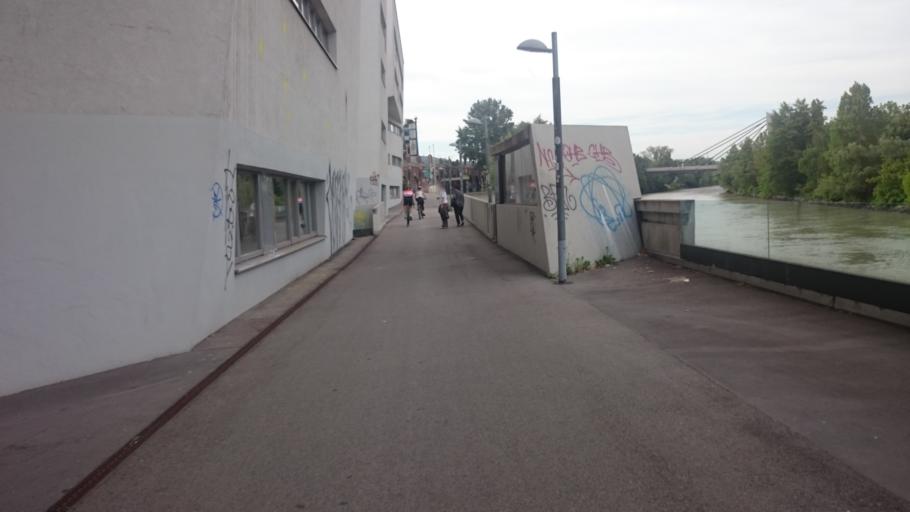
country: AT
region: Vienna
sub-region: Wien Stadt
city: Vienna
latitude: 48.2317
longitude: 16.3617
